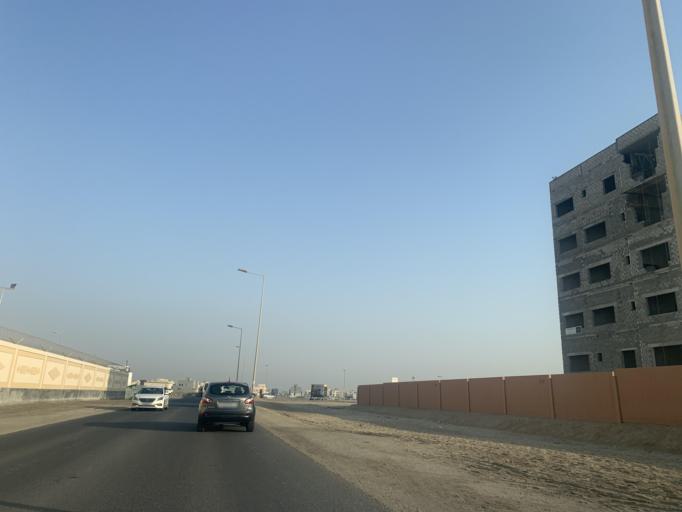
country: BH
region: Manama
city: Jidd Hafs
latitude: 26.2085
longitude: 50.5253
